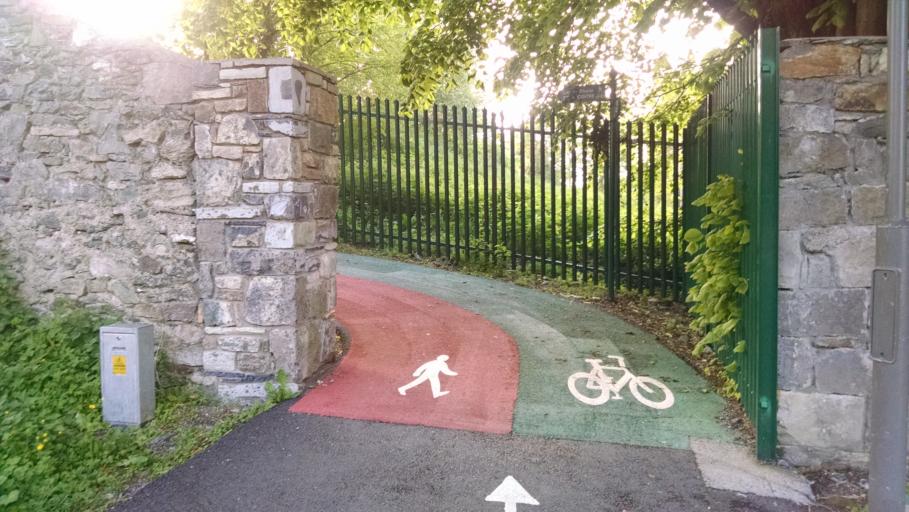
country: IE
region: Connaught
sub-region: Maigh Eo
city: Westport
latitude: 53.7991
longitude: -9.5133
